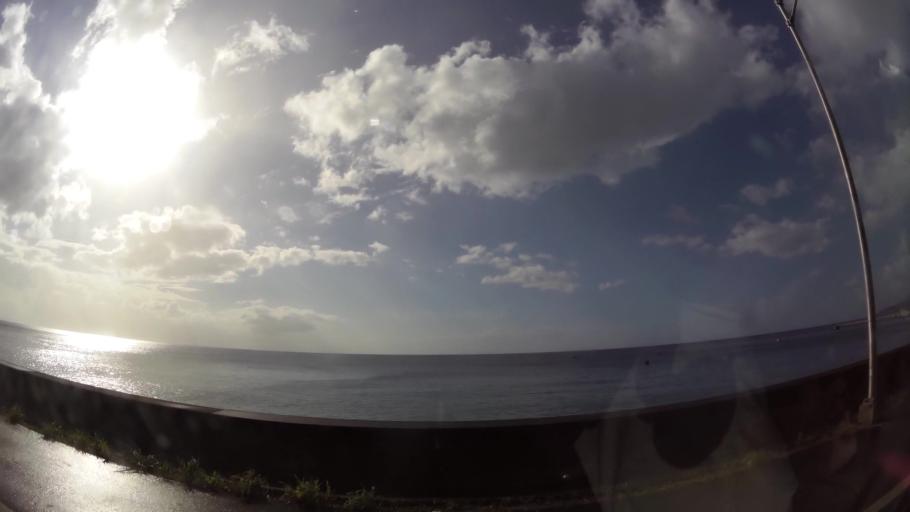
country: DM
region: Saint George
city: Roseau
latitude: 15.3269
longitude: -61.3953
